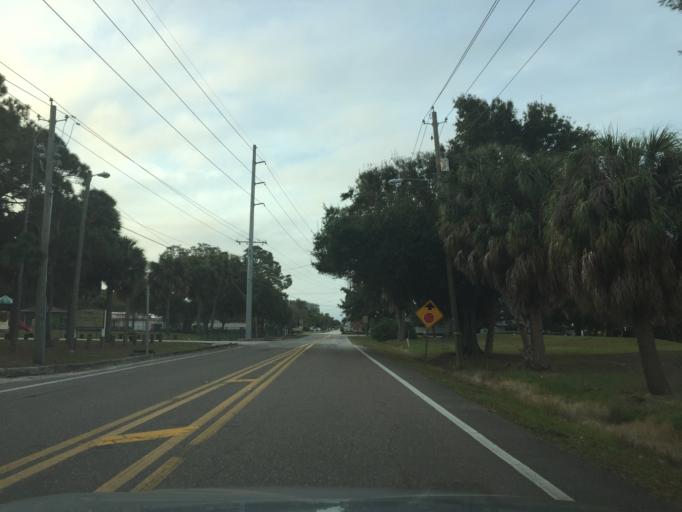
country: US
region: Florida
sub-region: Hillsborough County
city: Town 'n' Country
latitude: 27.9752
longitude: -82.5507
